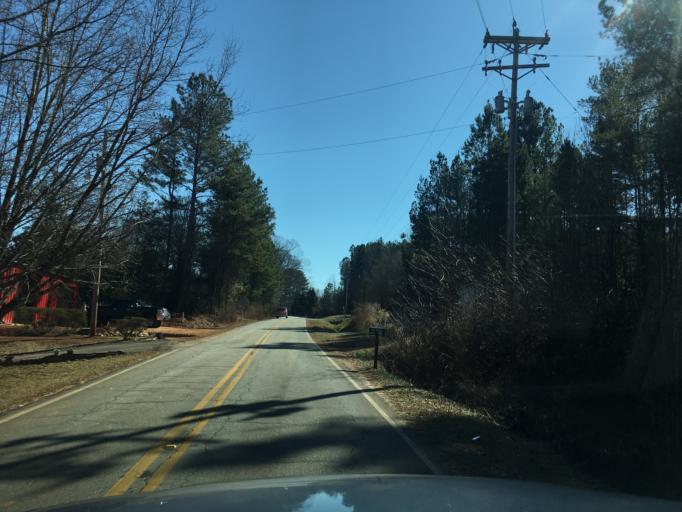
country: US
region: South Carolina
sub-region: Pickens County
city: Pickens
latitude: 34.8344
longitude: -82.7896
